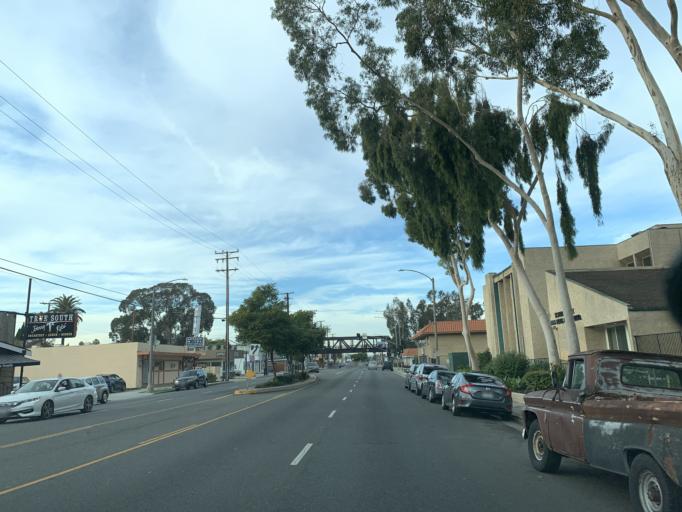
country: US
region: California
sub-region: Los Angeles County
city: Signal Hill
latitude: 33.8422
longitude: -118.1921
